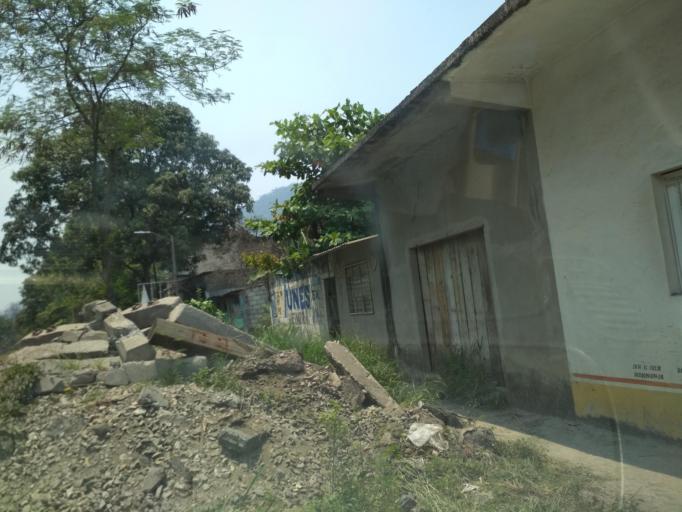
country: MX
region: Veracruz
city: Tezonapa
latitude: 18.6067
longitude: -96.6853
